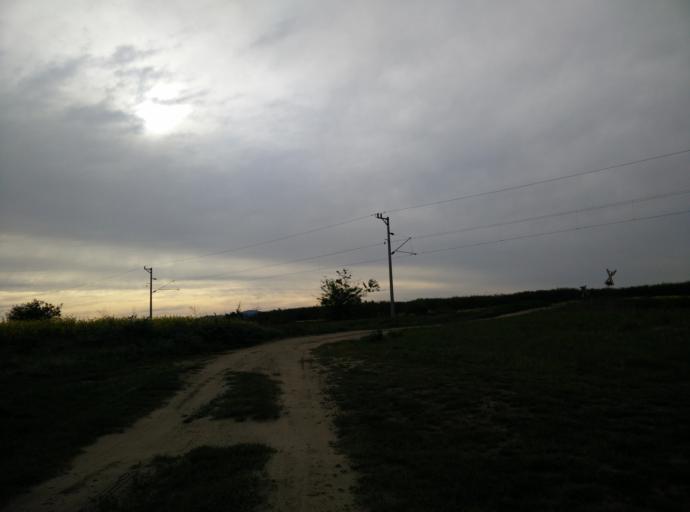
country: HU
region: Pest
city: Fot
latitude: 47.6079
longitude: 19.1654
